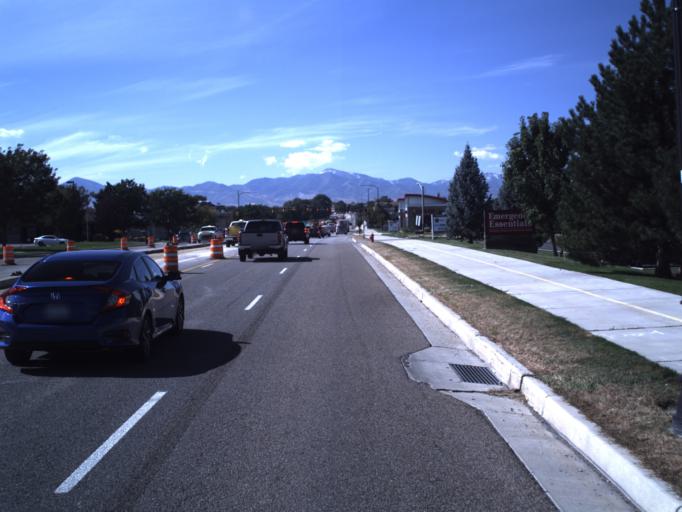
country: US
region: Utah
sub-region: Salt Lake County
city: South Jordan
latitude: 40.5600
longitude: -111.9175
